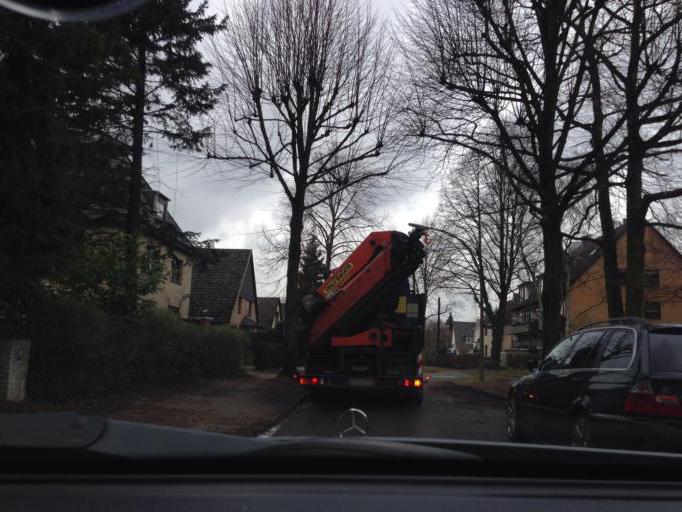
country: DE
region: Hamburg
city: Farmsen-Berne
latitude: 53.5853
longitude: 10.1148
